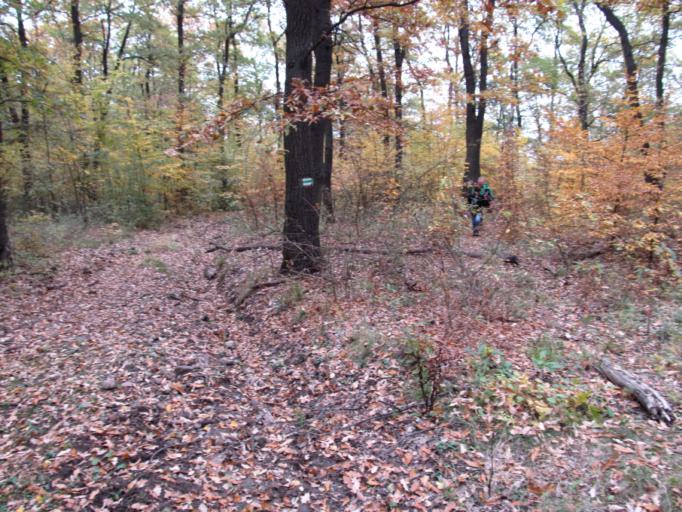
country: SK
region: Nitriansky
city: Sahy
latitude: 48.0401
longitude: 18.9762
